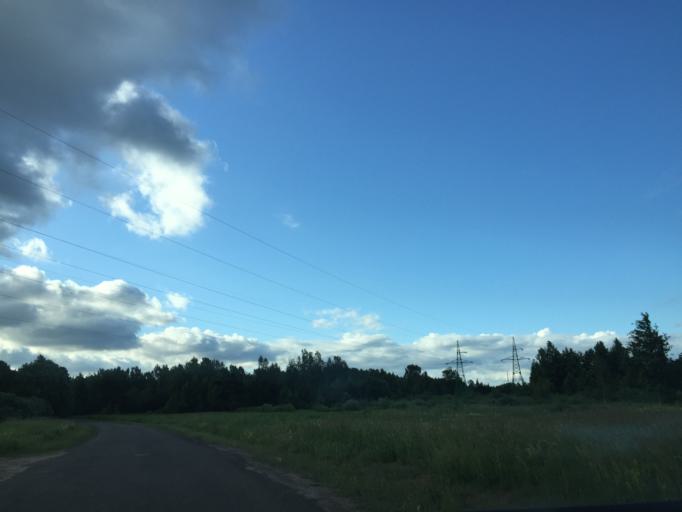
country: LV
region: Ventspils
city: Ventspils
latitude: 57.4098
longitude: 21.6178
